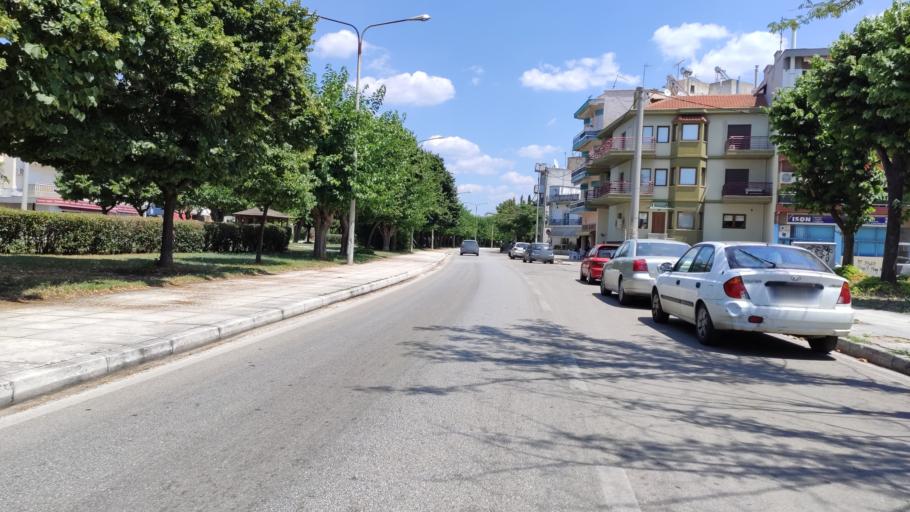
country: GR
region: East Macedonia and Thrace
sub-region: Nomos Rodopis
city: Komotini
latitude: 41.1158
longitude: 25.3942
